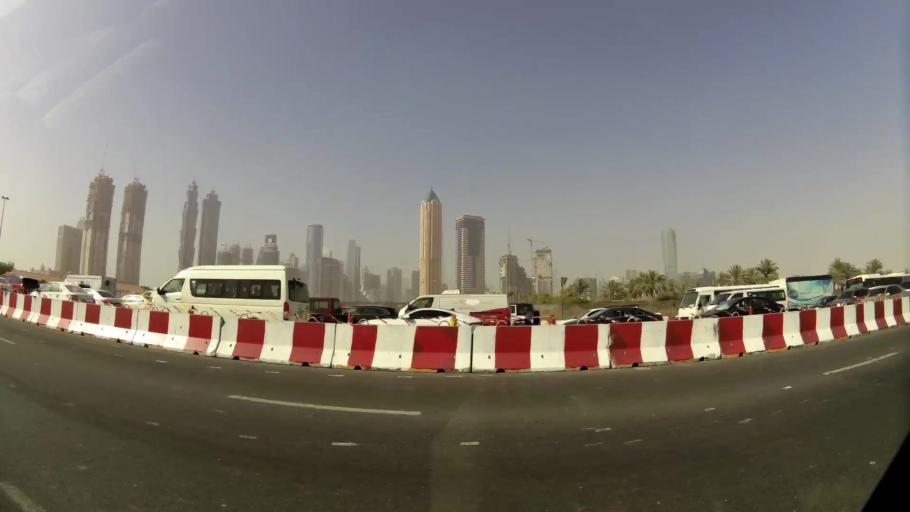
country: AE
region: Dubai
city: Dubai
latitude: 25.1744
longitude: 55.2577
